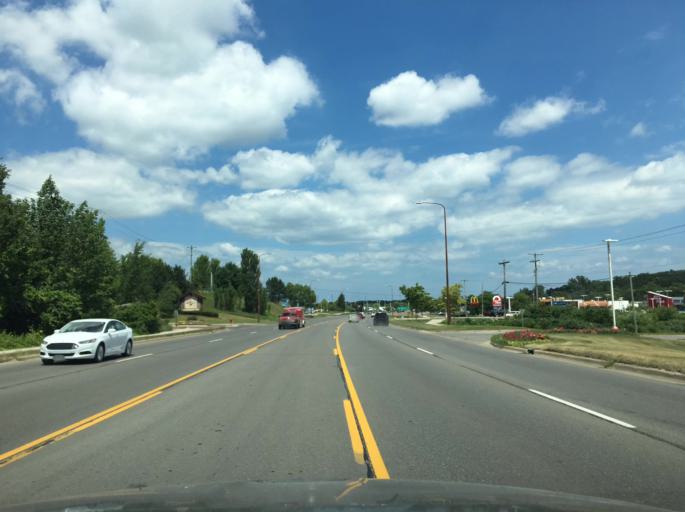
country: US
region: Michigan
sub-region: Grand Traverse County
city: Traverse City
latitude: 44.7372
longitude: -85.6455
